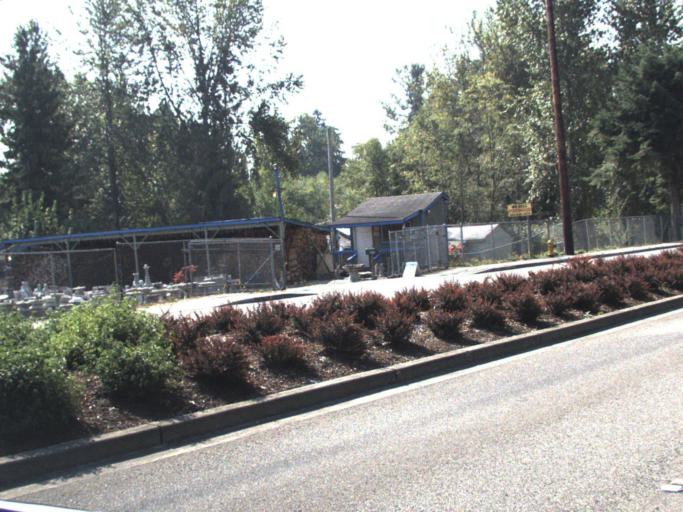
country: US
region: Washington
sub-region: King County
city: Federal Way
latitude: 47.3630
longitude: -122.3068
